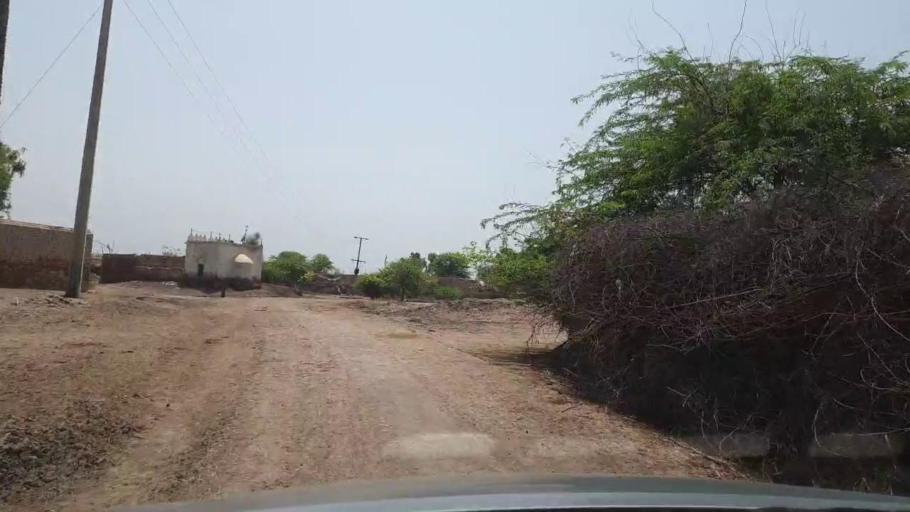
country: PK
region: Sindh
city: Madeji
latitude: 27.7740
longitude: 68.4053
